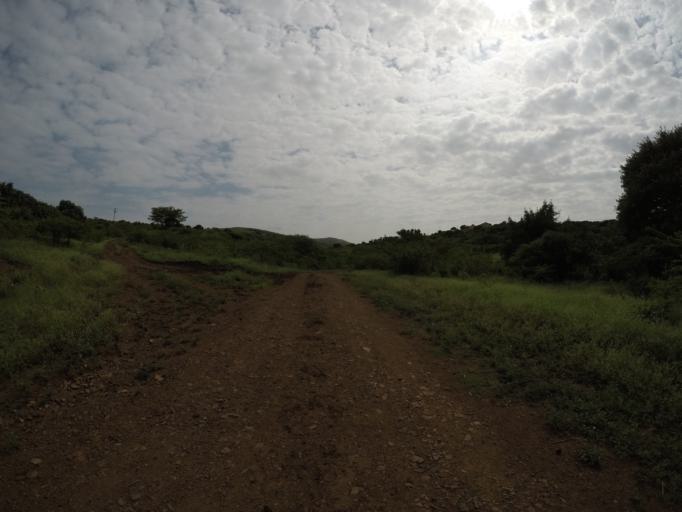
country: ZA
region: KwaZulu-Natal
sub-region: uThungulu District Municipality
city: Empangeni
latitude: -28.6275
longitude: 31.8943
